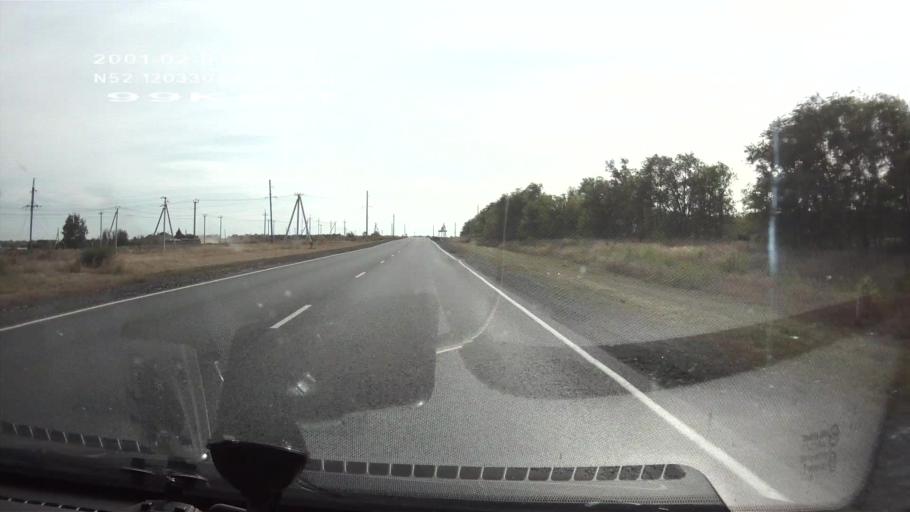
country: RU
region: Saratov
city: Balakovo
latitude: 52.1200
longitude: 47.7523
